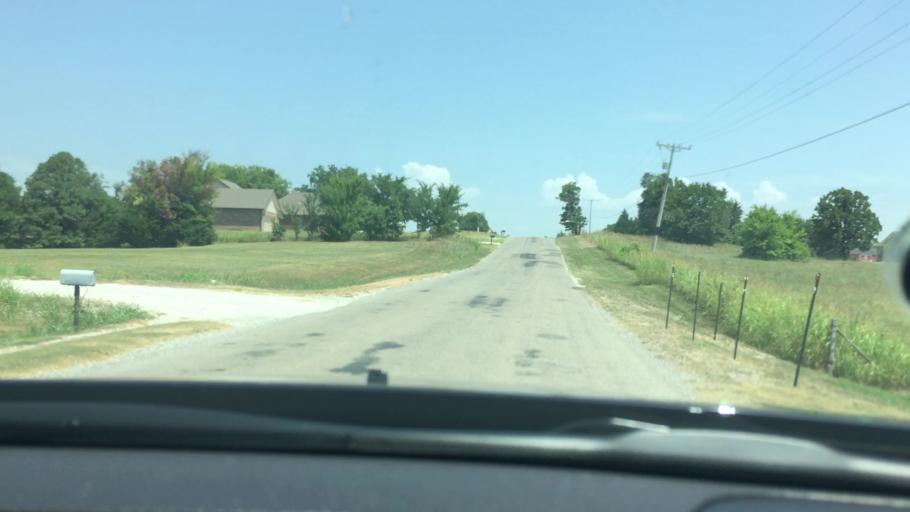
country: US
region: Oklahoma
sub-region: Pontotoc County
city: Byng
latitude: 34.8435
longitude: -96.6697
